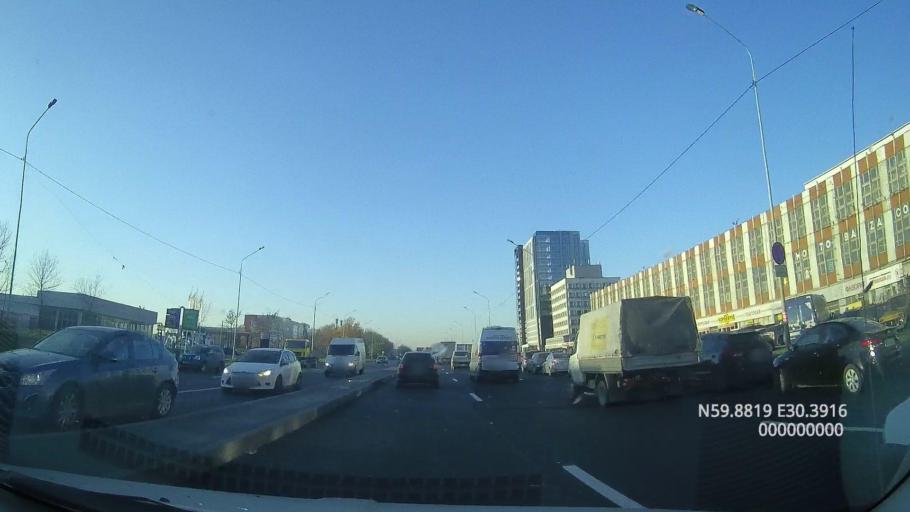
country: RU
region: St.-Petersburg
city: Kupchino
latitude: 59.8820
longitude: 30.3915
